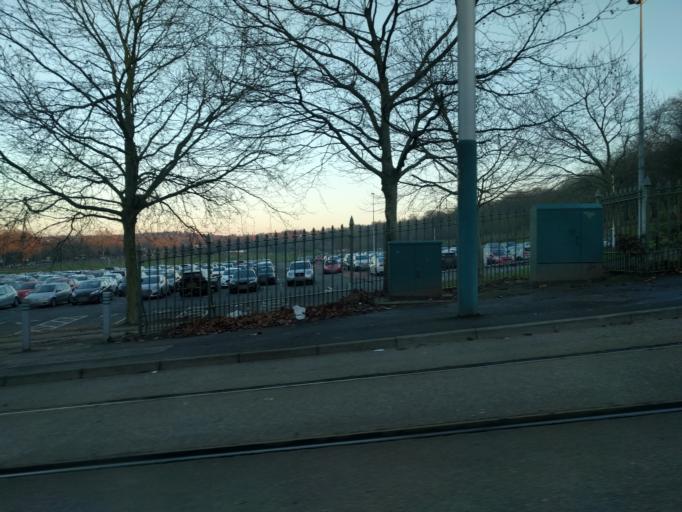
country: GB
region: England
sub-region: Nottingham
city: Nottingham
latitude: 52.9647
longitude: -1.1667
